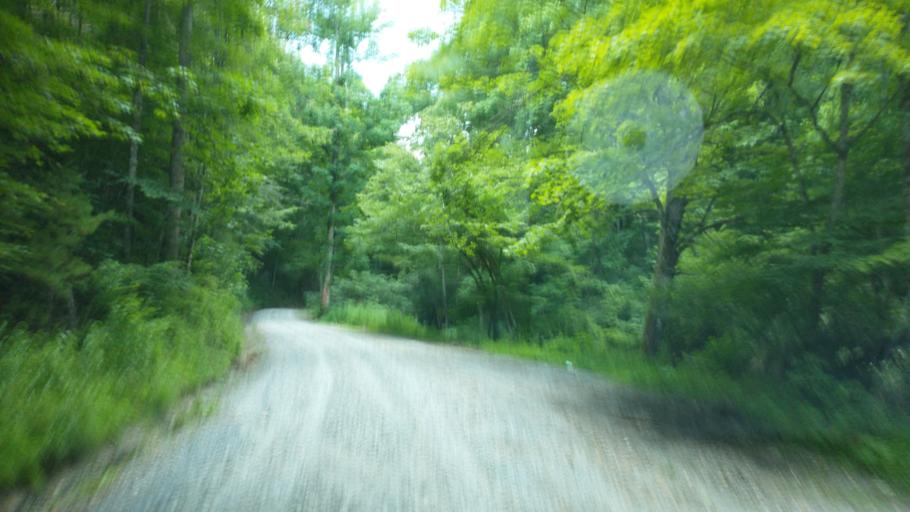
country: US
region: West Virginia
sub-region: Mercer County
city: Athens
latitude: 37.4299
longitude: -80.9972
